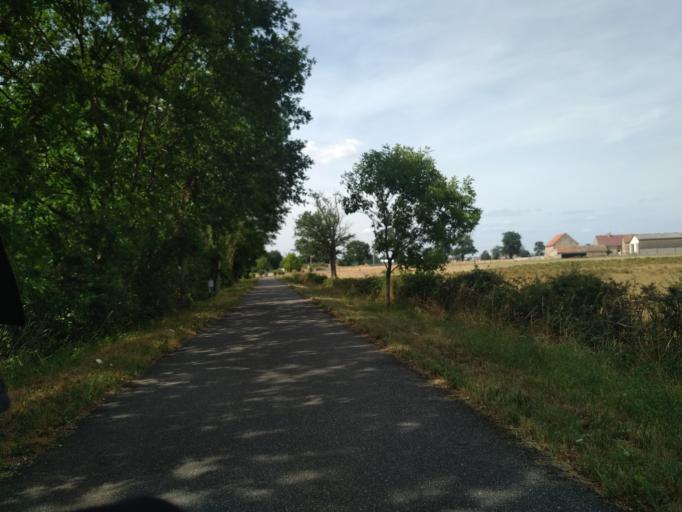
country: FR
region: Bourgogne
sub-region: Departement de Saone-et-Loire
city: Bourbon-Lancy
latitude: 46.6104
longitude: 3.7438
